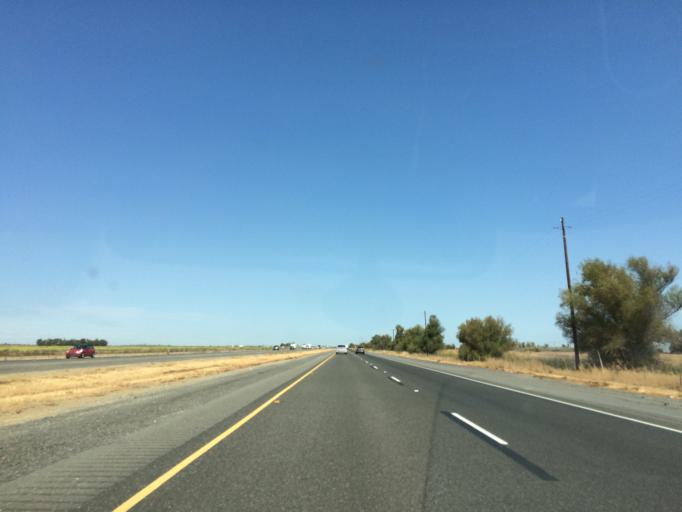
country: US
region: California
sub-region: Glenn County
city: Willows
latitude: 39.4368
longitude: -122.1933
